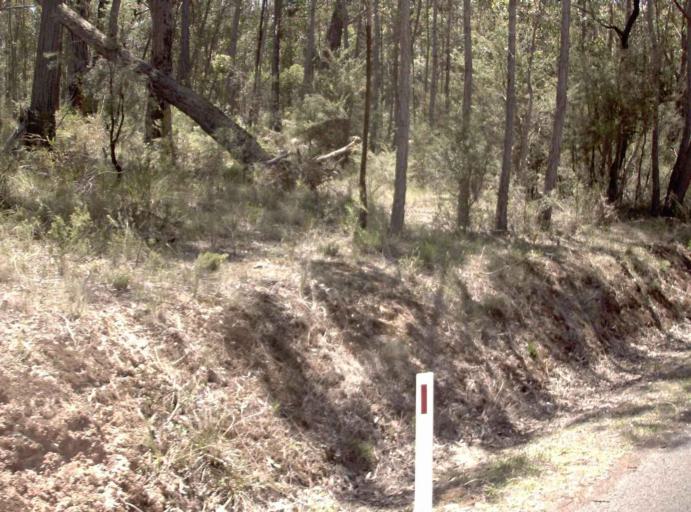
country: AU
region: Victoria
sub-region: East Gippsland
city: Lakes Entrance
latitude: -37.7562
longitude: 148.0643
